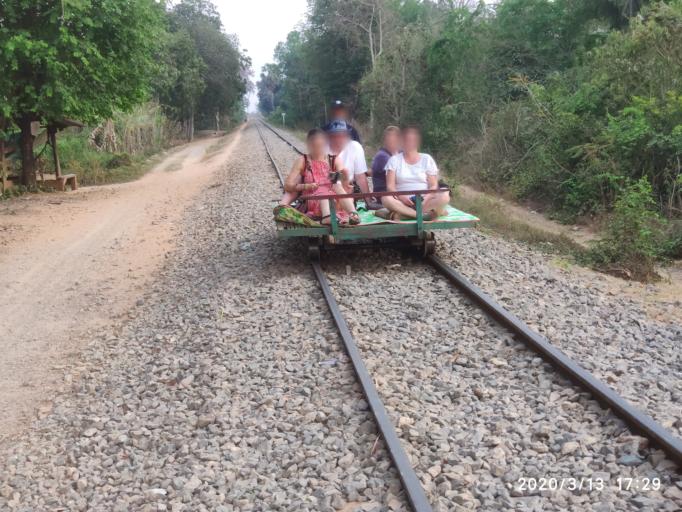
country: KH
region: Battambang
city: Battambang
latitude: 13.0687
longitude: 103.2174
